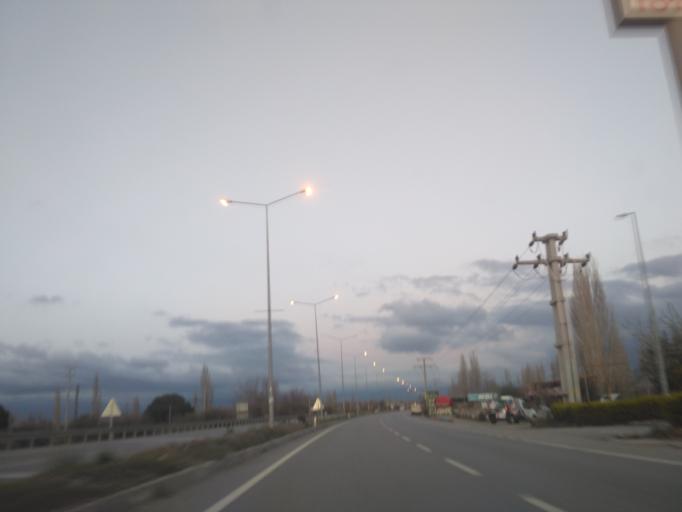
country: TR
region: Balikesir
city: Burhaniye
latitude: 39.5135
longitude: 26.9775
